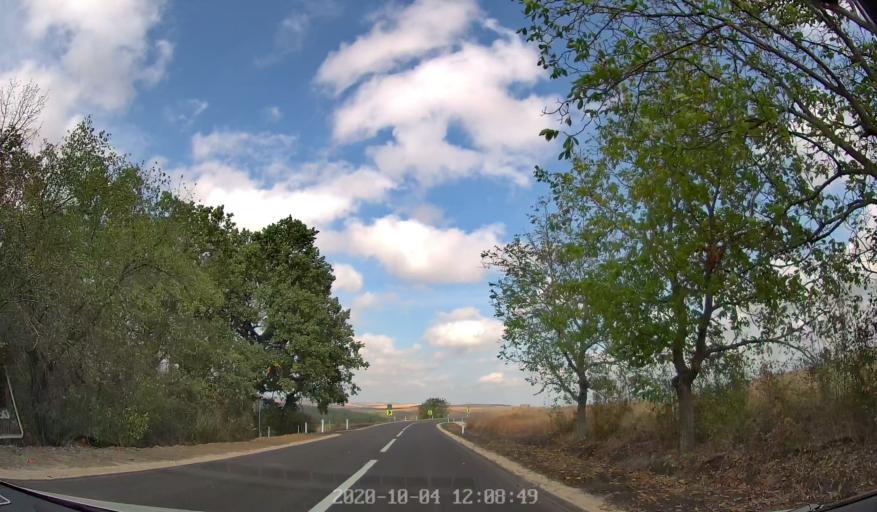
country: MD
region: Rezina
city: Saharna
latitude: 47.5986
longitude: 28.9758
